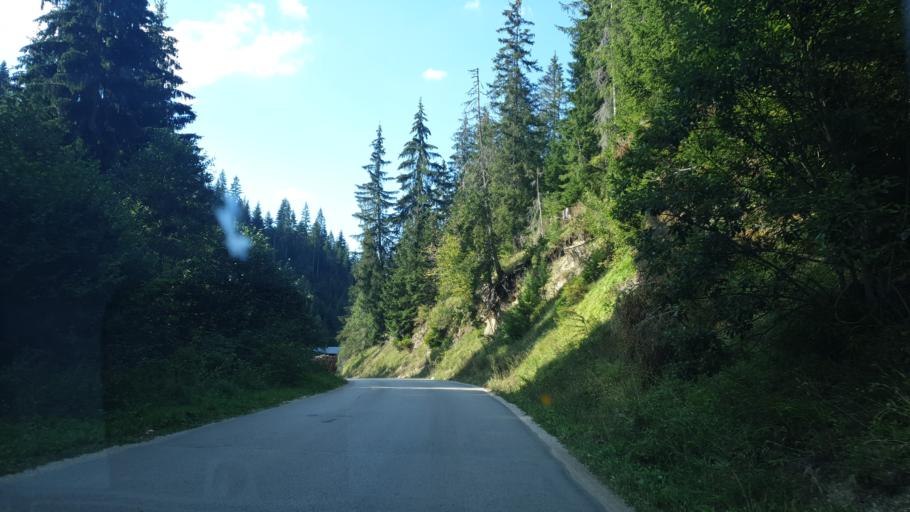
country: RS
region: Central Serbia
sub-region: Zlatiborski Okrug
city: Nova Varos
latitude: 43.4462
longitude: 19.8499
